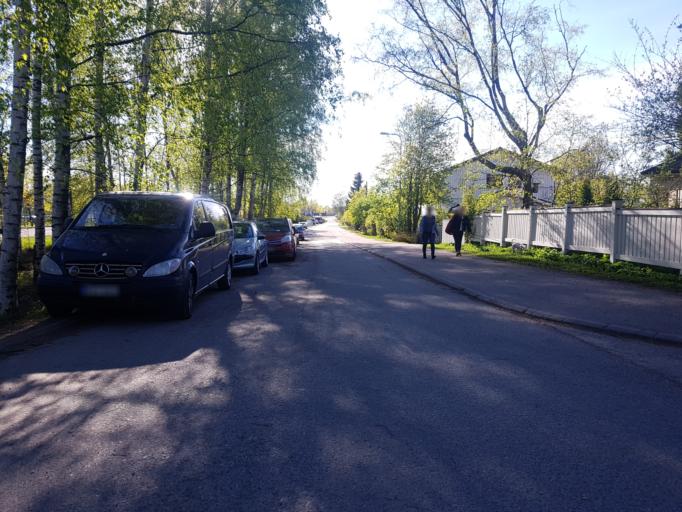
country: FI
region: Uusimaa
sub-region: Helsinki
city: Vantaa
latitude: 60.2782
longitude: 25.0251
